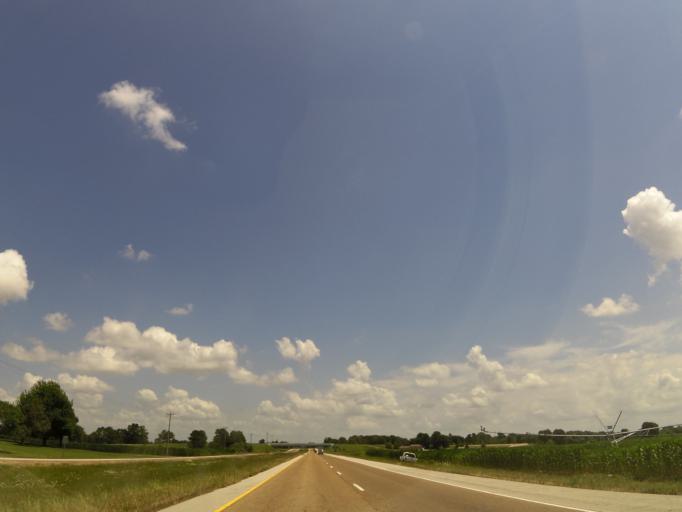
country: US
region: Tennessee
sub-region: Crockett County
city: Alamo
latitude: 35.8222
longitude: -89.1707
